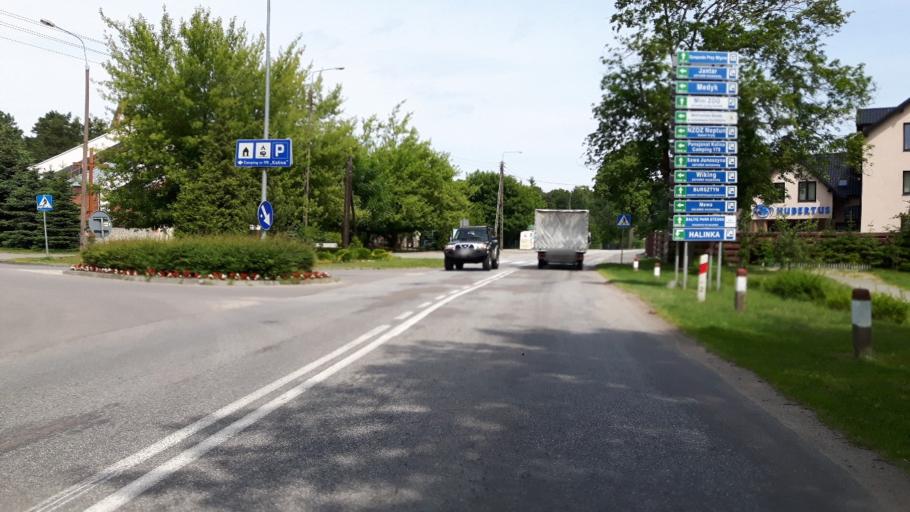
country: PL
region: Pomeranian Voivodeship
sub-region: Powiat nowodworski
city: Stegna
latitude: 54.3321
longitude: 19.0330
